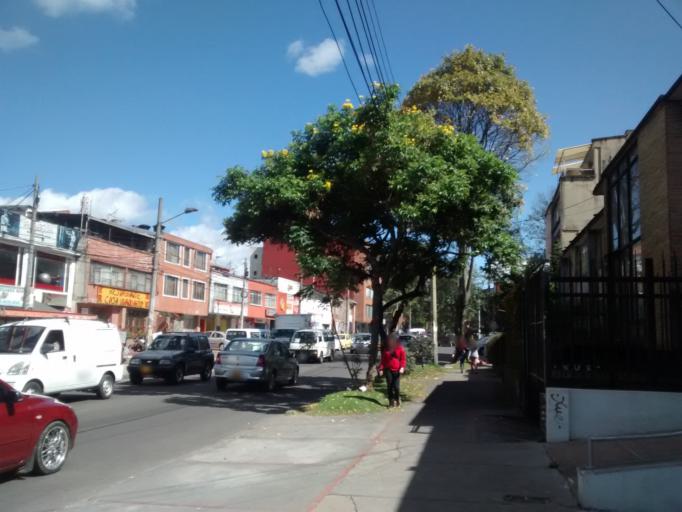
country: CO
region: Bogota D.C.
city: Bogota
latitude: 4.6351
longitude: -74.0752
